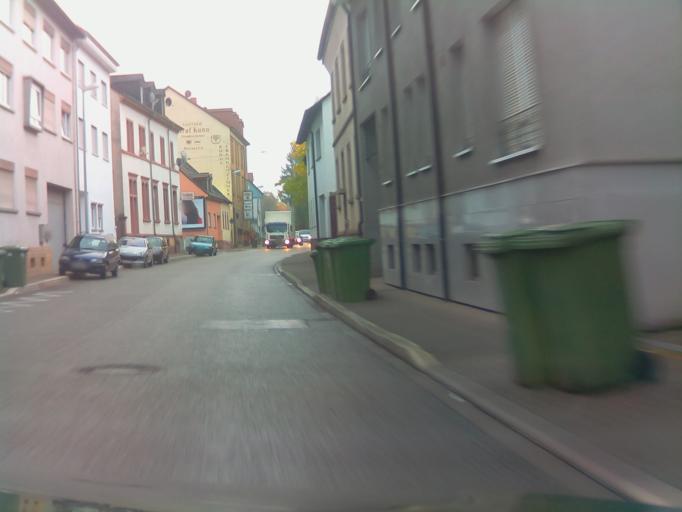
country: DE
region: Baden-Wuerttemberg
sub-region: Karlsruhe Region
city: Bruchsal
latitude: 49.1210
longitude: 8.6055
